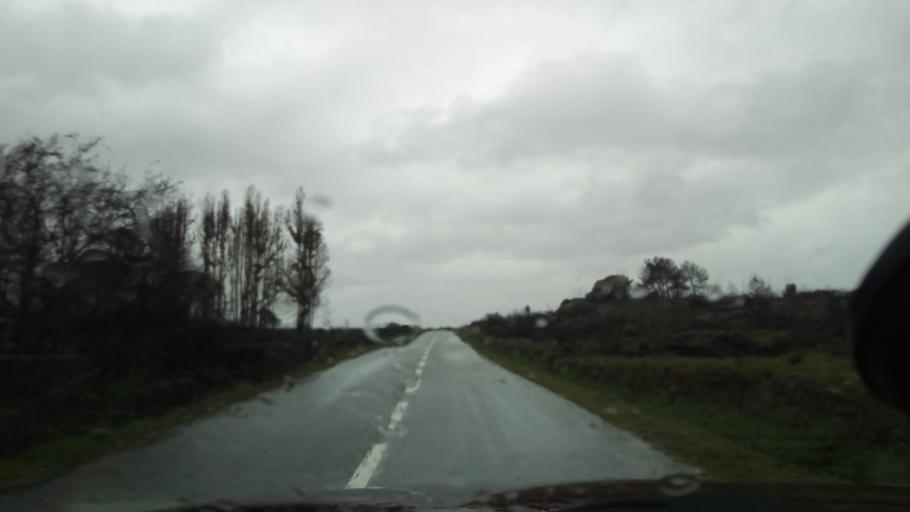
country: PT
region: Guarda
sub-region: Fornos de Algodres
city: Fornos de Algodres
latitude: 40.5594
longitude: -7.5187
